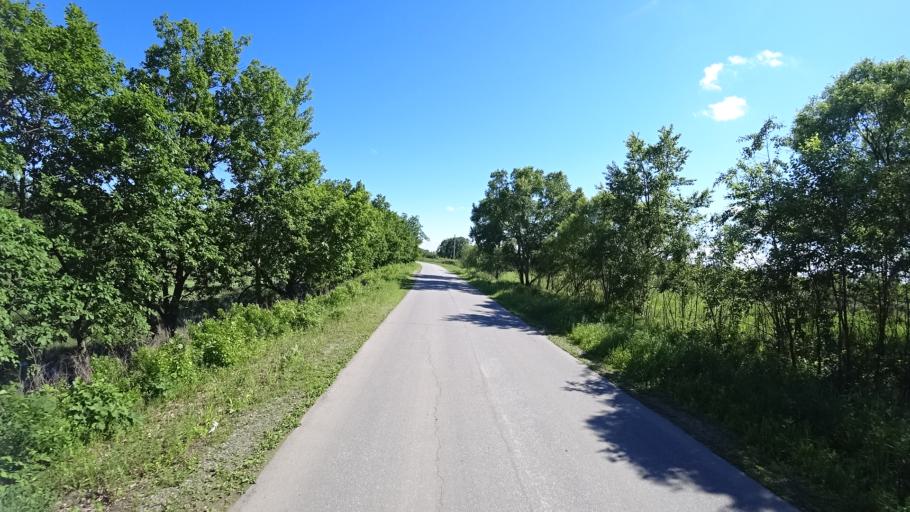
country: RU
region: Khabarovsk Krai
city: Khor
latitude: 47.8928
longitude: 135.0226
